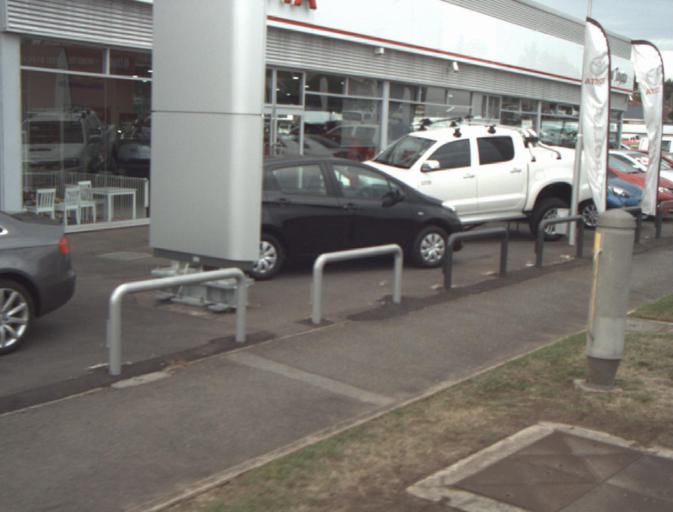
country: AU
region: Tasmania
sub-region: Launceston
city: East Launceston
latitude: -41.4648
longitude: 147.1588
